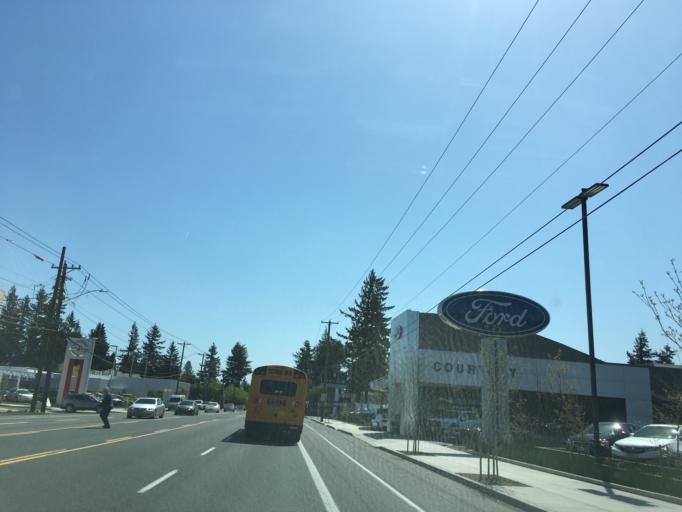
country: US
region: Oregon
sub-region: Multnomah County
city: Lents
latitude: 45.5330
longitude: -122.5374
